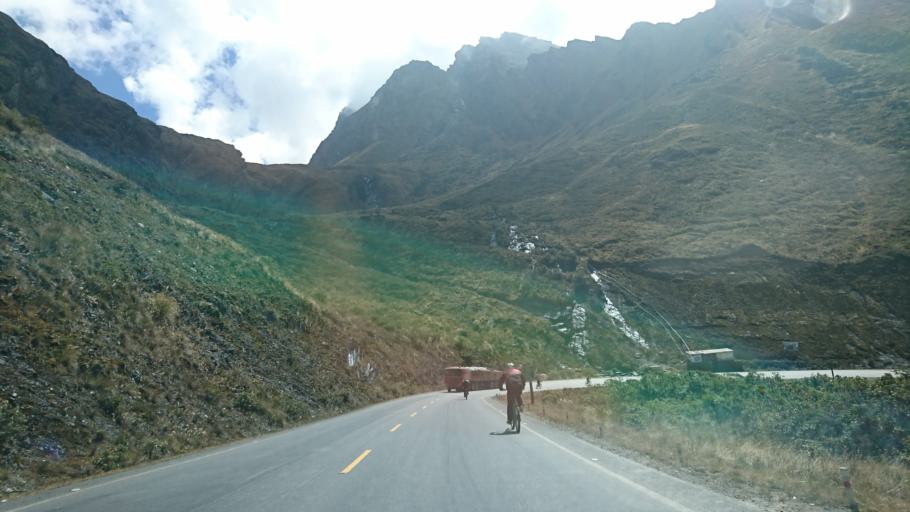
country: BO
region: La Paz
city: La Paz
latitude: -16.3280
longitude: -67.9565
